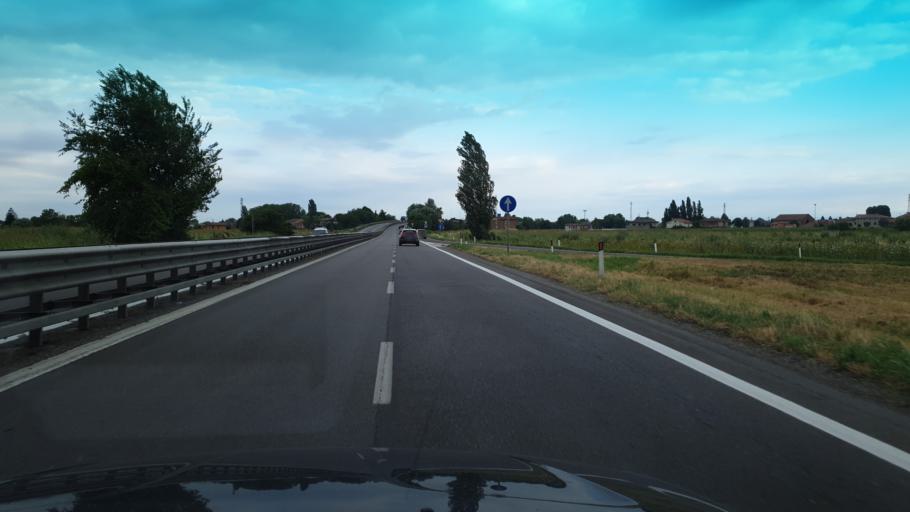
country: IT
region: Veneto
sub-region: Provincia di Verona
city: Legnago
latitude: 45.1800
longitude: 11.2759
